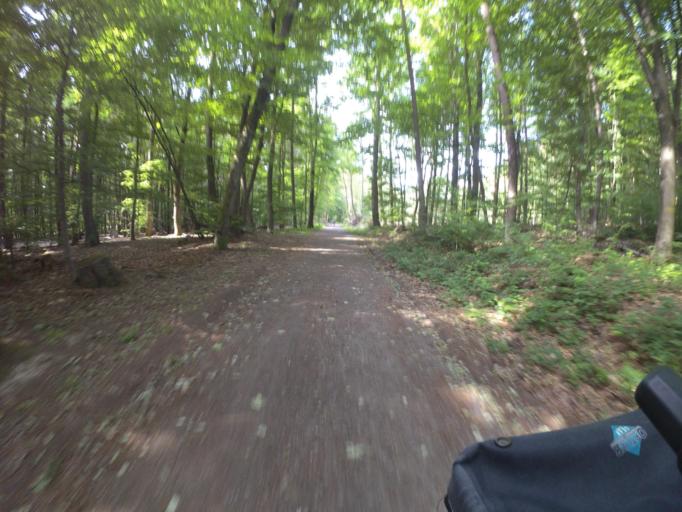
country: DE
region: Rheinland-Pfalz
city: Mackenbach
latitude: 49.4660
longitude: 7.5825
